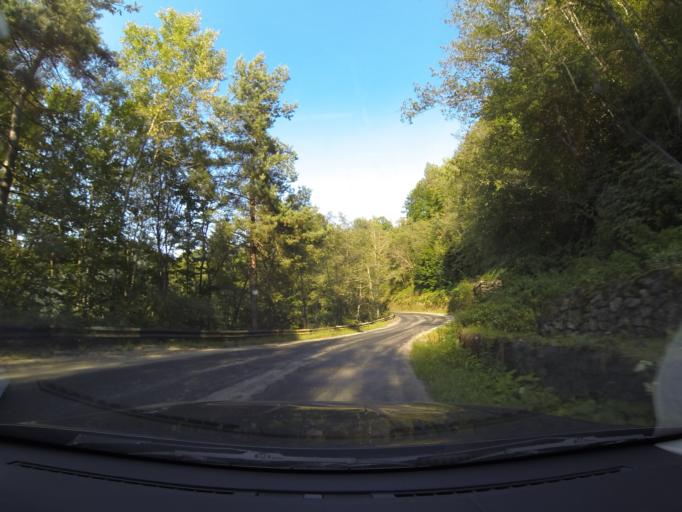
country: RO
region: Arges
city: Poenari
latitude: 45.3651
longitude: 24.6438
